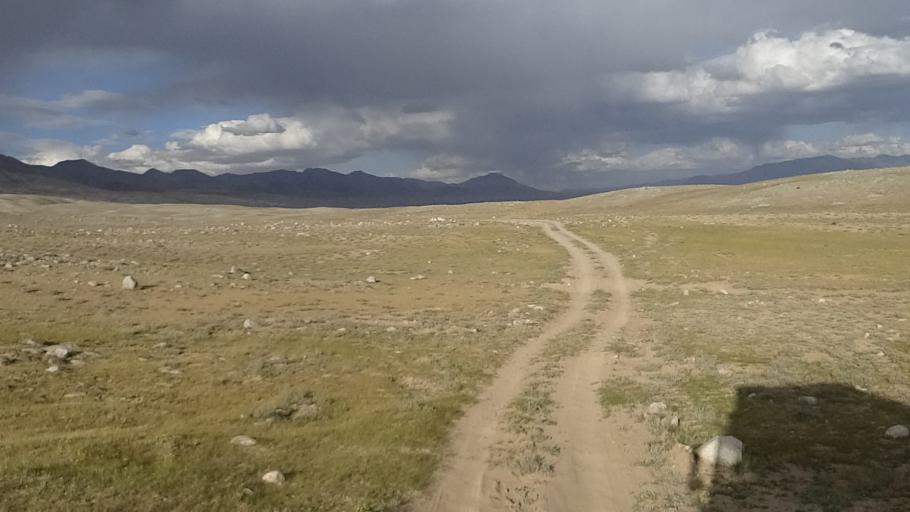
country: TJ
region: Gorno-Badakhshan
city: Murghob
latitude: 37.4619
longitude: 73.6184
